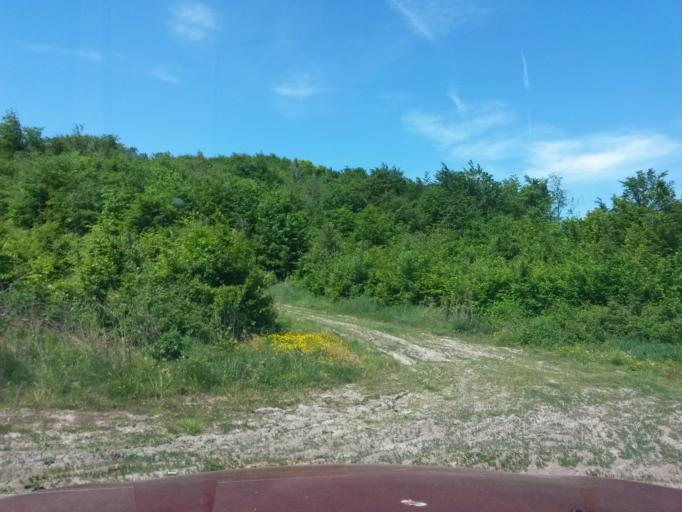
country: SK
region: Presovsky
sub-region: Okres Presov
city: Presov
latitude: 48.8787
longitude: 21.3904
